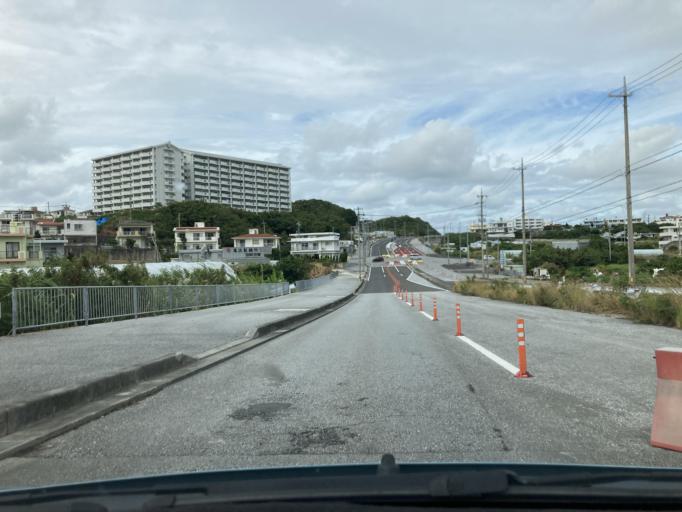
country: JP
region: Okinawa
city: Tomigusuku
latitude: 26.1647
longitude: 127.6788
